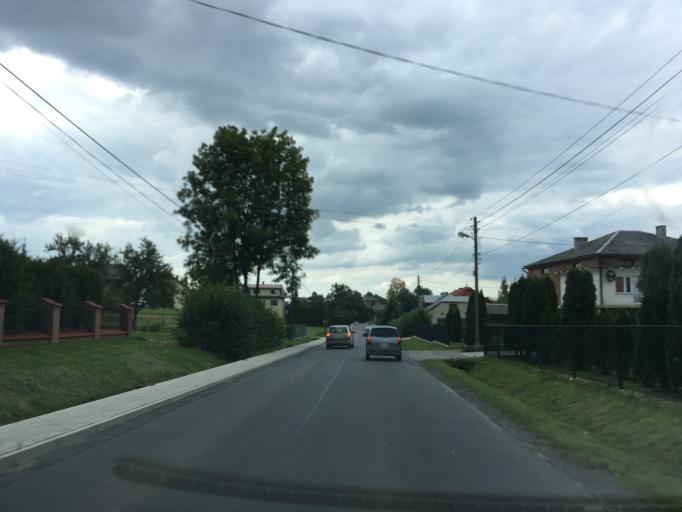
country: PL
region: Lesser Poland Voivodeship
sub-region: Powiat olkuski
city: Wolbrom
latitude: 50.4035
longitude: 19.7673
